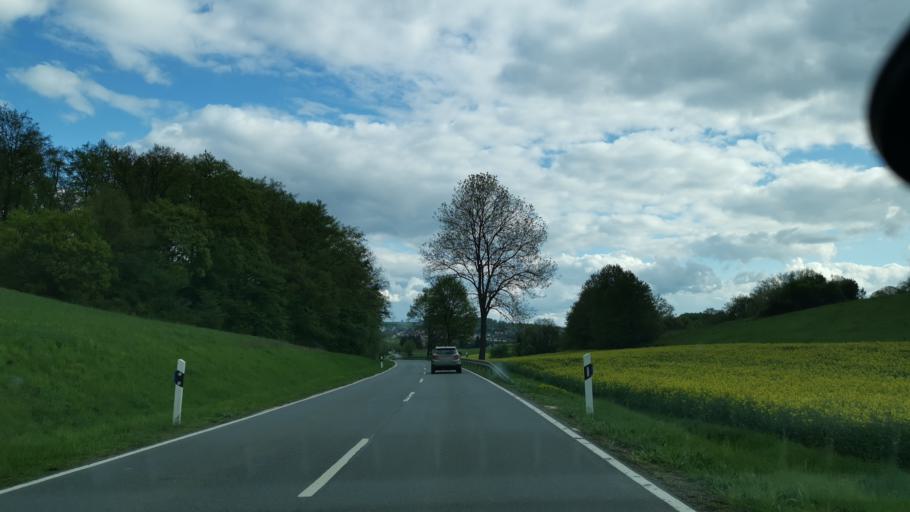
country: DE
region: Baden-Wuerttemberg
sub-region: Karlsruhe Region
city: Osterburken
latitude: 49.4459
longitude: 9.4268
